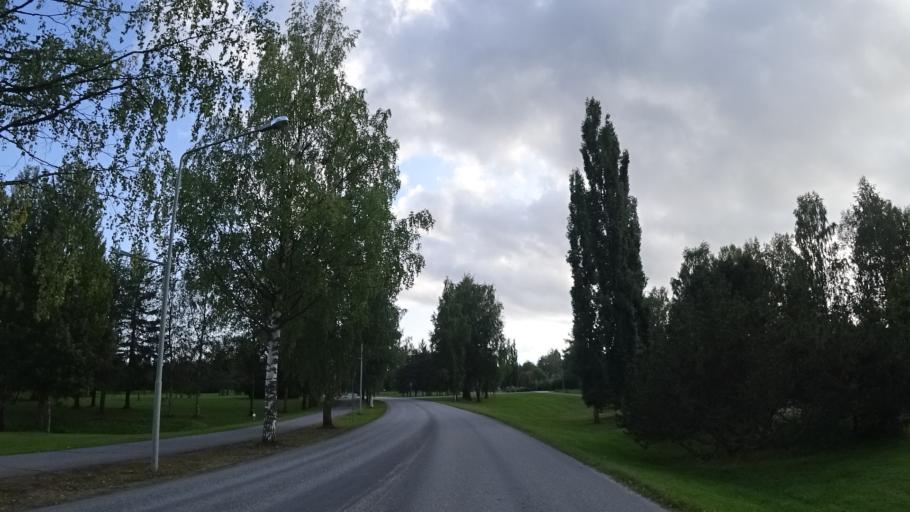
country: FI
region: North Karelia
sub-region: Pielisen Karjala
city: Lieksa
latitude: 63.3293
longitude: 30.0241
